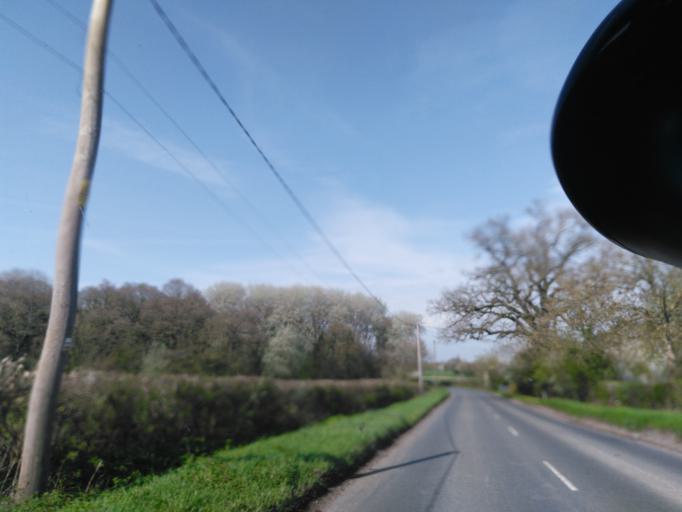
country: GB
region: England
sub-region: Wiltshire
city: Wingfield
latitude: 51.3016
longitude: -2.2595
